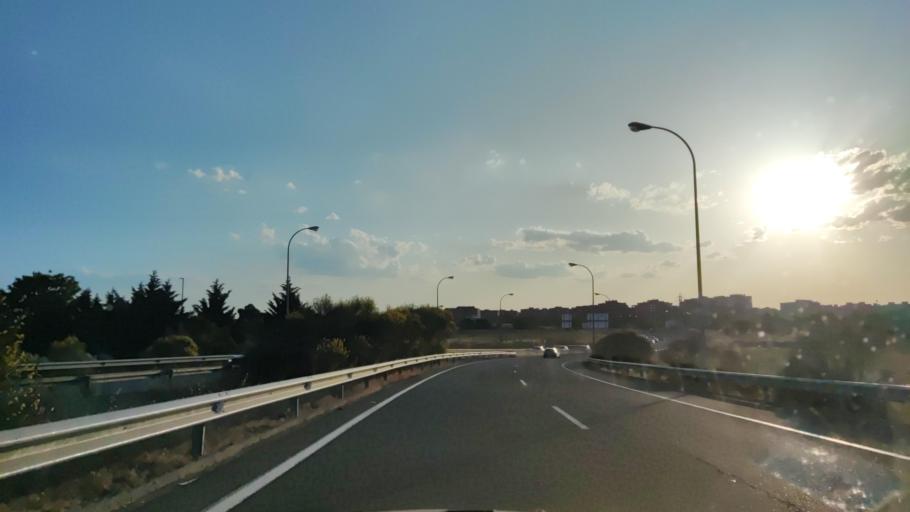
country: ES
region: Madrid
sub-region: Provincia de Madrid
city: Getafe
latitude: 40.3340
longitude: -3.7301
